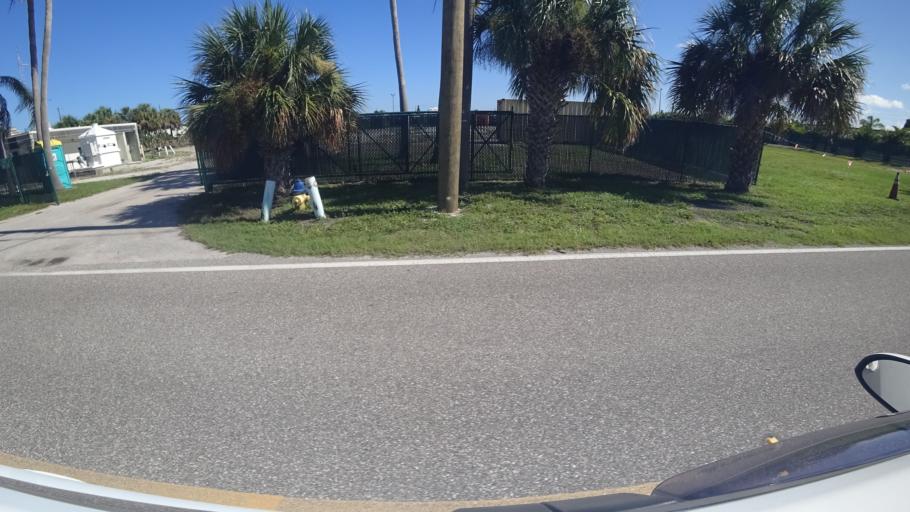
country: US
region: Florida
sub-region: Manatee County
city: Bayshore Gardens
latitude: 27.4184
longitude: -82.5822
